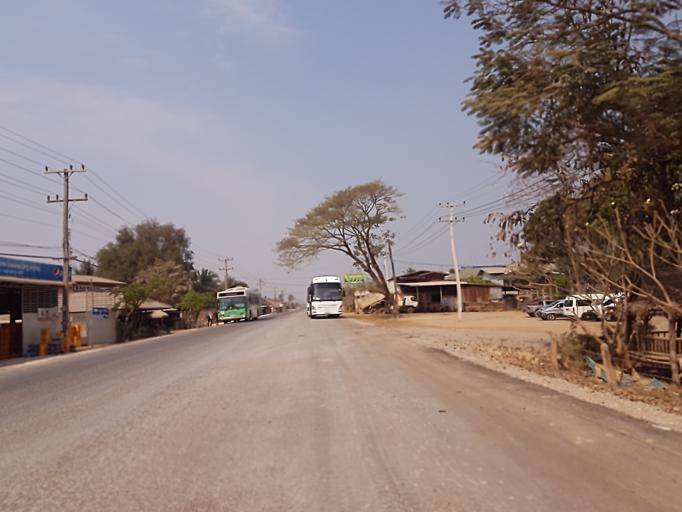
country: TH
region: Nong Khai
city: Nong Khai
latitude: 17.9128
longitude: 102.7642
